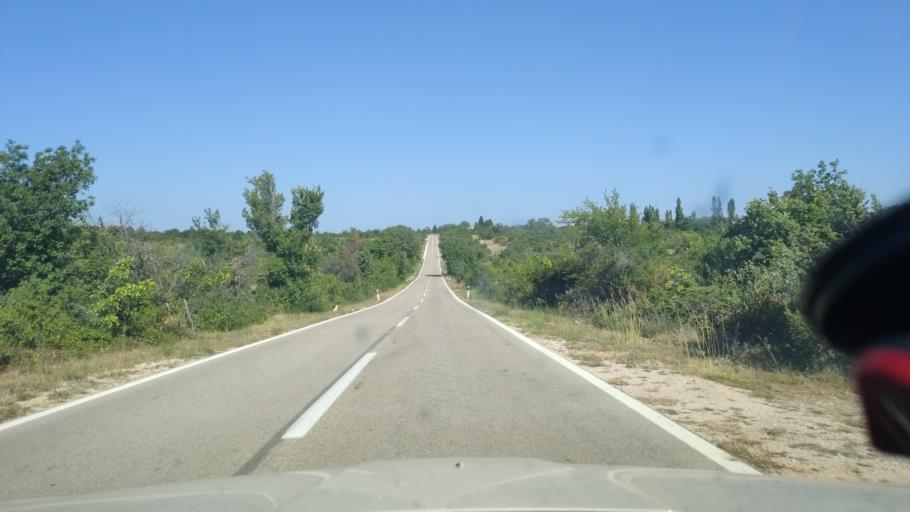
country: HR
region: Sibensko-Kniniska
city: Zaton
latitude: 43.9082
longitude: 15.8546
